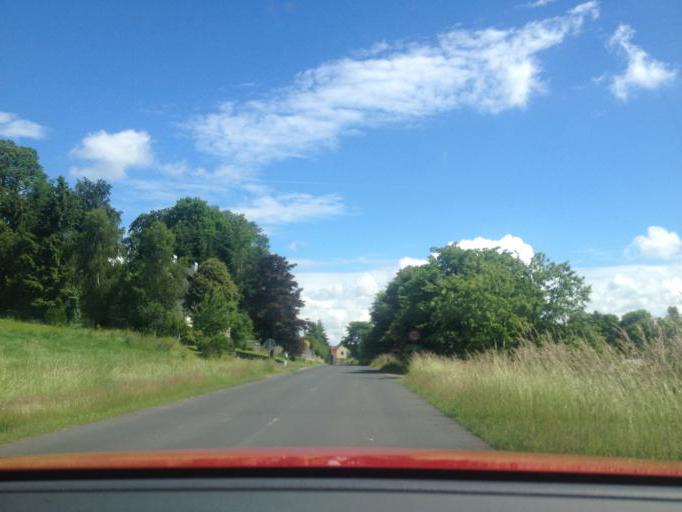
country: DE
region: Bavaria
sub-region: Upper Palatinate
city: Pechbrunn
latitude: 49.9995
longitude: 12.1912
